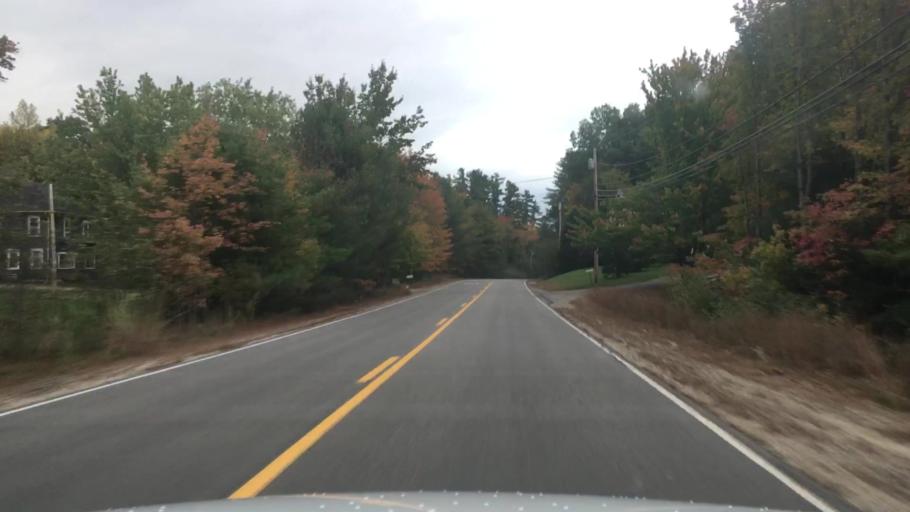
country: US
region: Maine
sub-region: York County
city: Hollis Center
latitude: 43.6049
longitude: -70.5893
